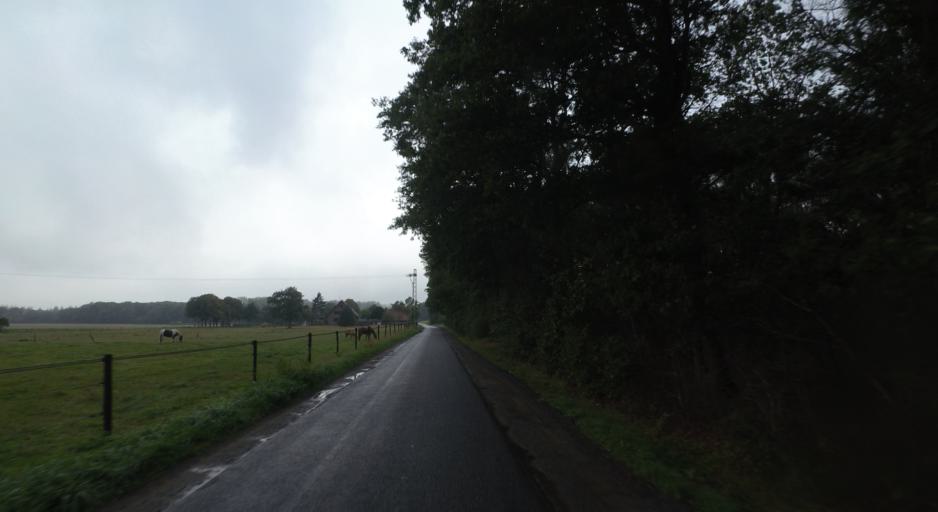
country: DE
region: North Rhine-Westphalia
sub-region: Regierungsbezirk Dusseldorf
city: Hamminkeln
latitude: 51.7077
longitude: 6.6199
